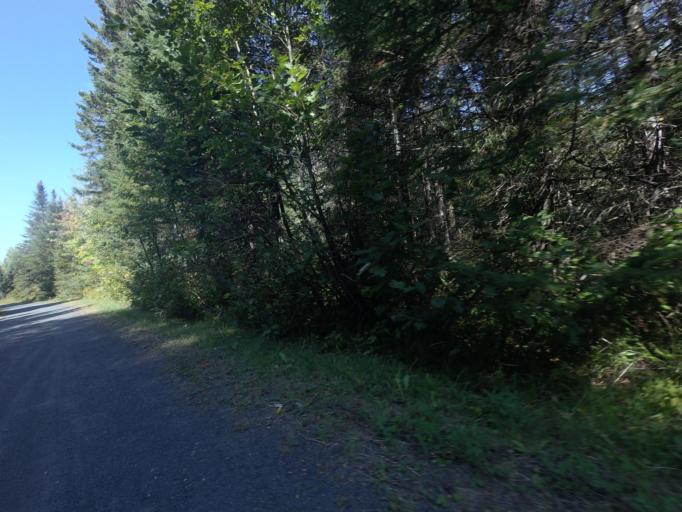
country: CA
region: Quebec
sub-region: Laurentides
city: Sainte-Agathe-des-Monts
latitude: 46.0596
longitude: -74.2880
